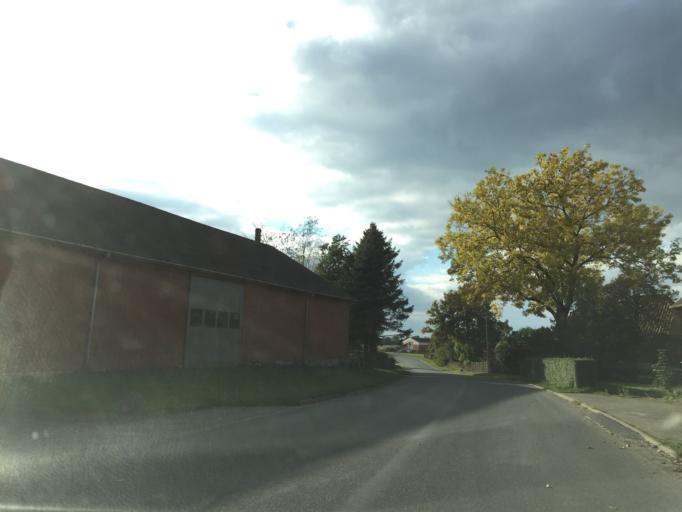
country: DK
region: Central Jutland
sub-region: Favrskov Kommune
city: Hammel
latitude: 56.2832
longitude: 9.7631
